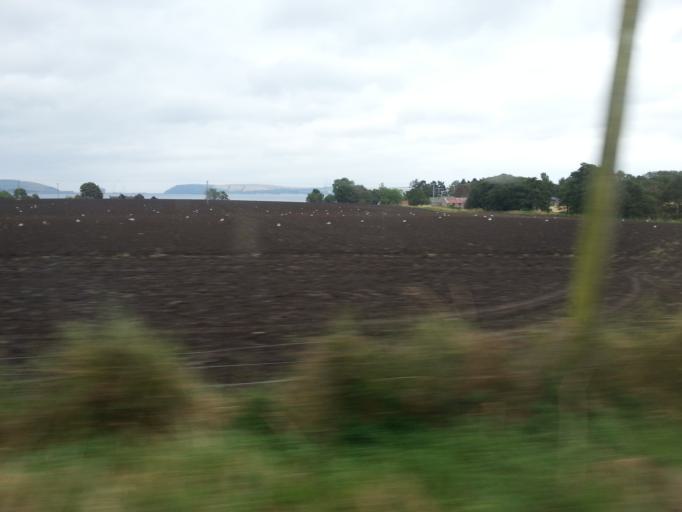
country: GB
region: Scotland
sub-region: Highland
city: Invergordon
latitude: 57.7224
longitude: -4.1131
